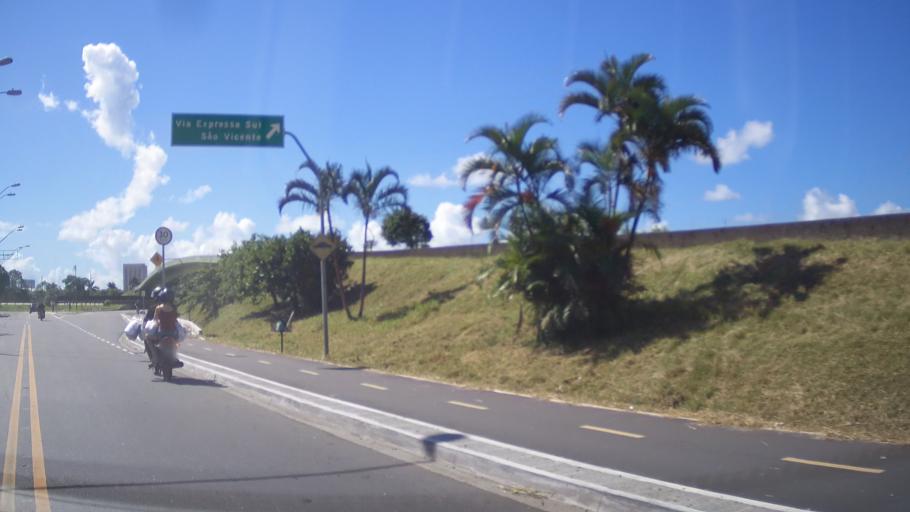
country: BR
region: Sao Paulo
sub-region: Praia Grande
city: Praia Grande
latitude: -24.0313
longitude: -46.5111
